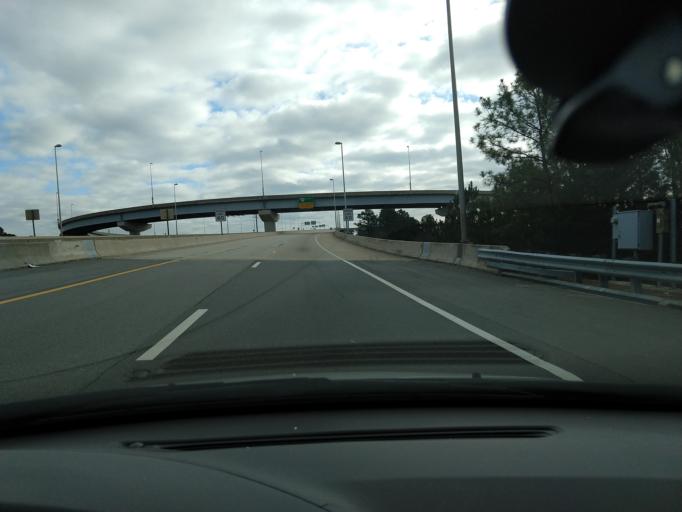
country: US
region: Virginia
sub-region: Chesterfield County
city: Bensley
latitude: 37.4441
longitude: -77.4327
